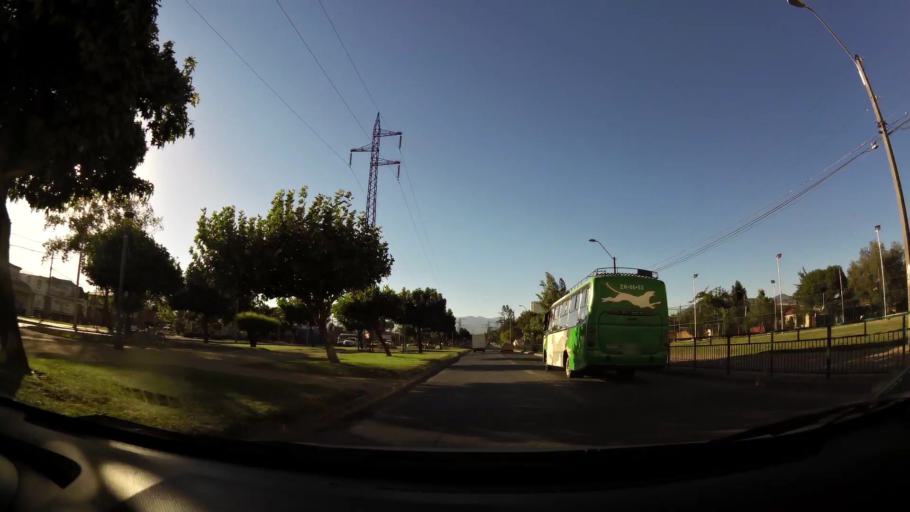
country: CL
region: O'Higgins
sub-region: Provincia de Cachapoal
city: Rancagua
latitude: -34.1727
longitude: -70.7149
